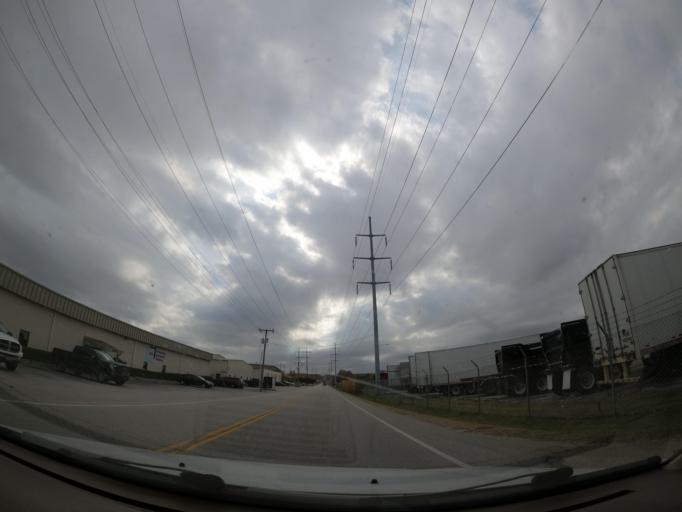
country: US
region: Oklahoma
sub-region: Tulsa County
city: Tulsa
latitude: 36.1004
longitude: -95.9935
